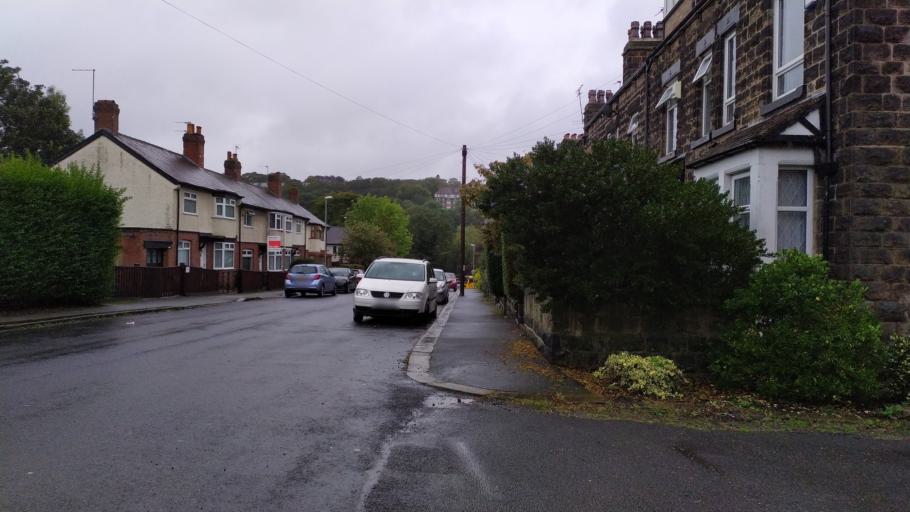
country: GB
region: England
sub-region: City and Borough of Leeds
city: Chapel Allerton
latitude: 53.8248
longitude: -1.5663
